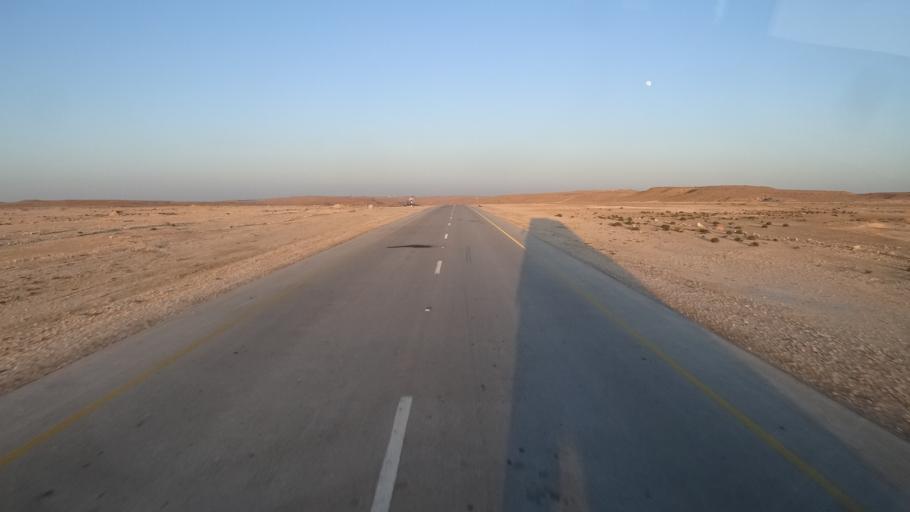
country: YE
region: Al Mahrah
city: Hawf
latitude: 16.9479
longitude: 53.3170
